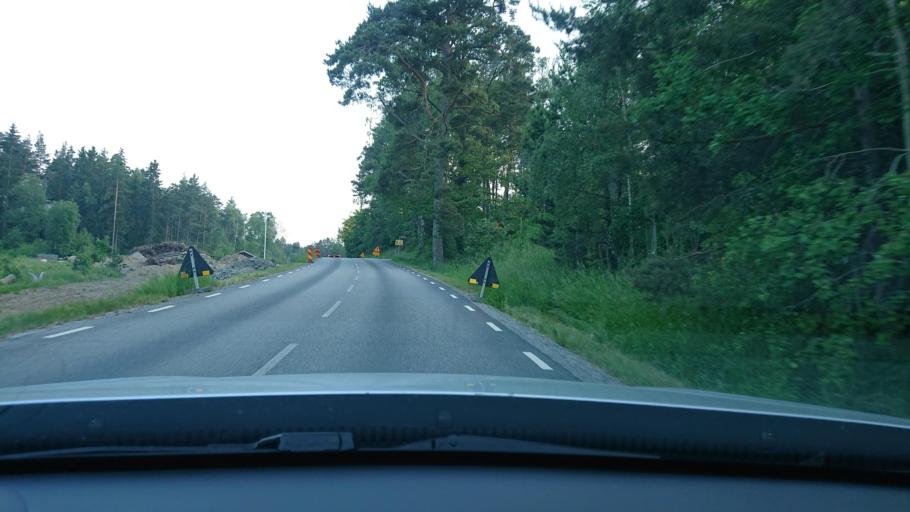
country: SE
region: Stockholm
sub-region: Vaxholms Kommun
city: Resaro
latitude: 59.4669
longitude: 18.3596
